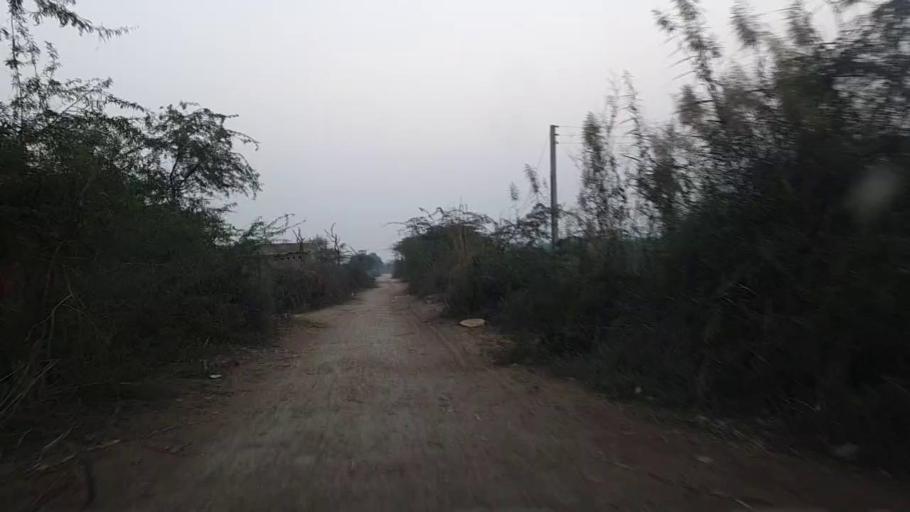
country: PK
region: Sindh
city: Karaundi
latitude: 26.9489
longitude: 68.4492
